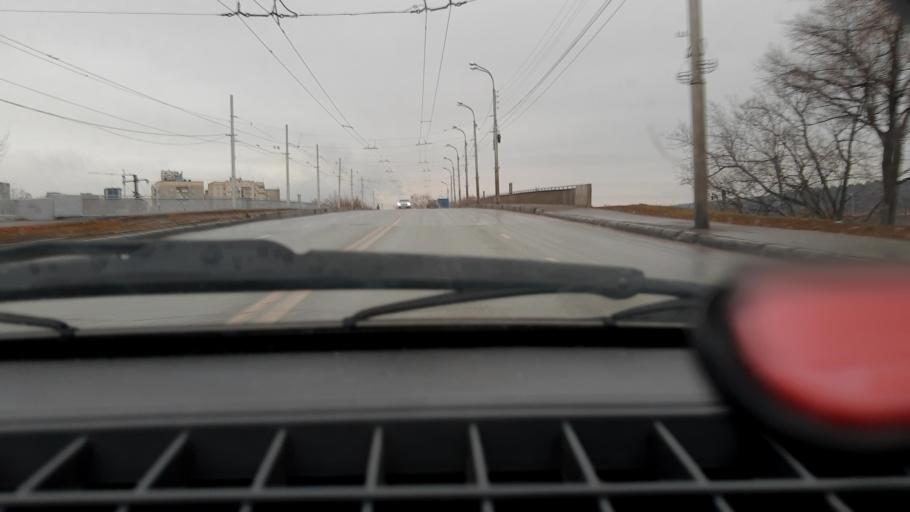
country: RU
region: Bashkortostan
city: Ufa
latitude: 54.7998
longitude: 56.1390
